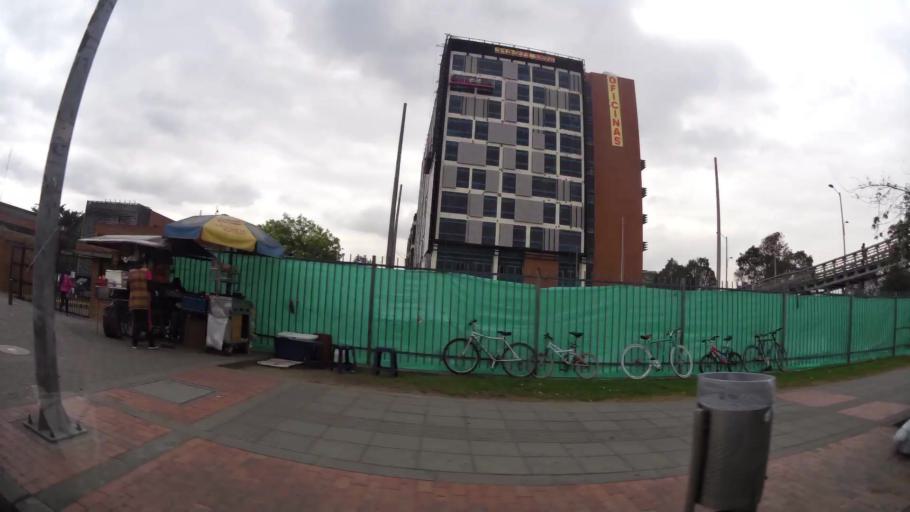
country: CO
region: Bogota D.C.
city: Bogota
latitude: 4.6736
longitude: -74.1167
